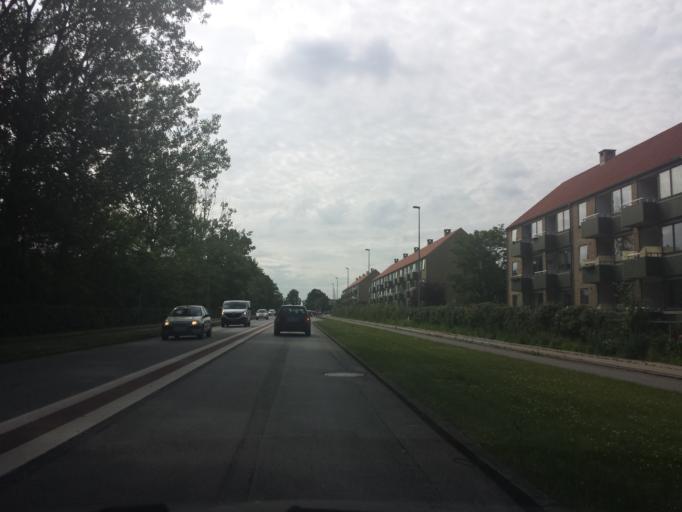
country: DK
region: Capital Region
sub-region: Ballerup Kommune
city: Ballerup
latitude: 55.7235
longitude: 12.3611
